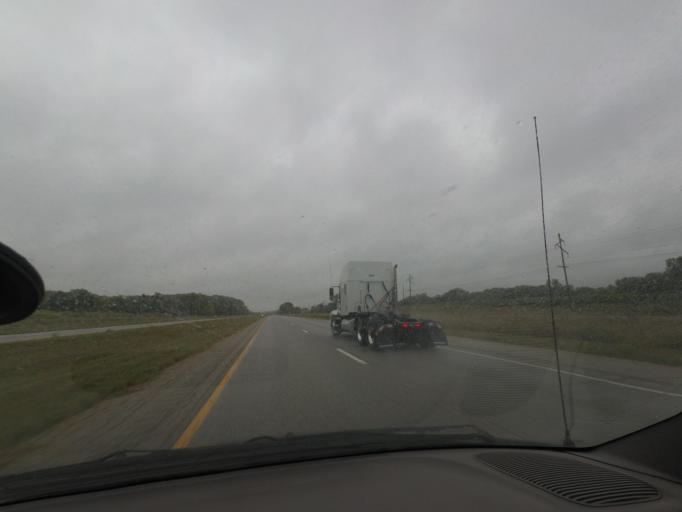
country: US
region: Illinois
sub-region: Pike County
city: Barry
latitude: 39.7128
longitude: -91.0950
